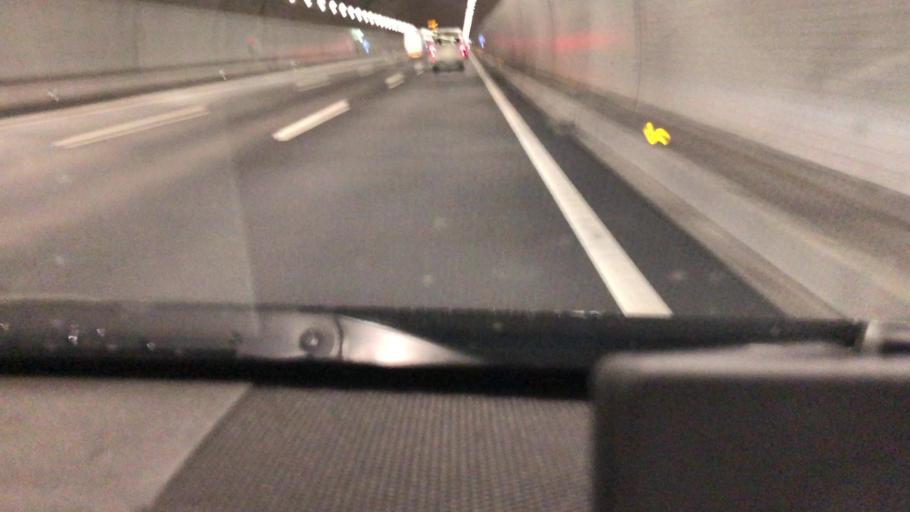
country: JP
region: Shizuoka
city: Kanaya
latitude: 34.8437
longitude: 138.0630
